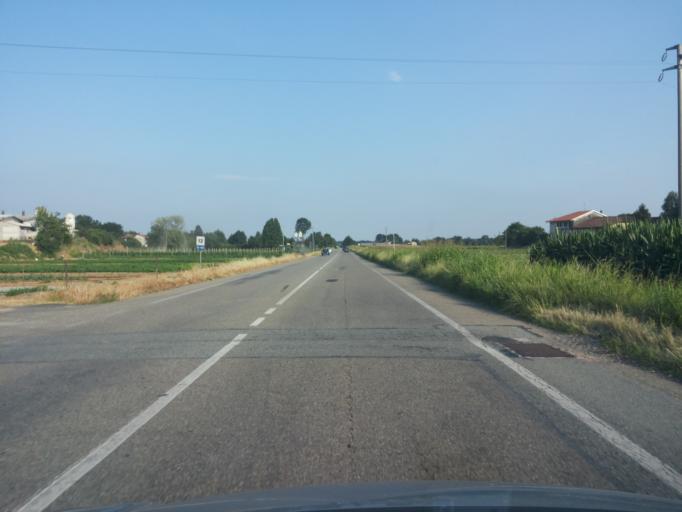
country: IT
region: Piedmont
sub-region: Provincia di Biella
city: Cavaglia
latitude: 45.4014
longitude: 8.1101
